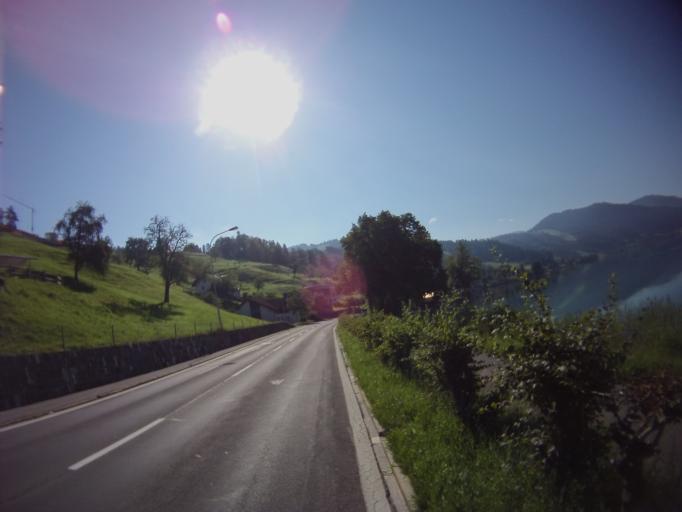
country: CH
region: Zug
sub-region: Zug
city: Unterageri
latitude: 47.1319
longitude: 8.6245
